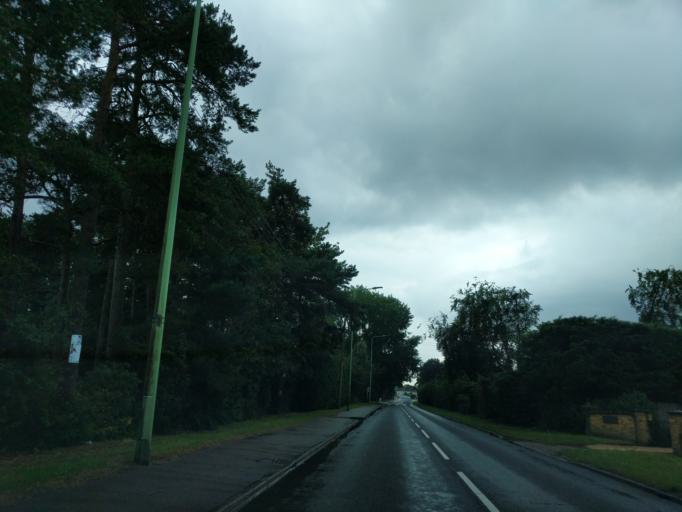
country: GB
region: England
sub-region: Suffolk
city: Lakenheath
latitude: 52.3538
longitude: 0.5134
